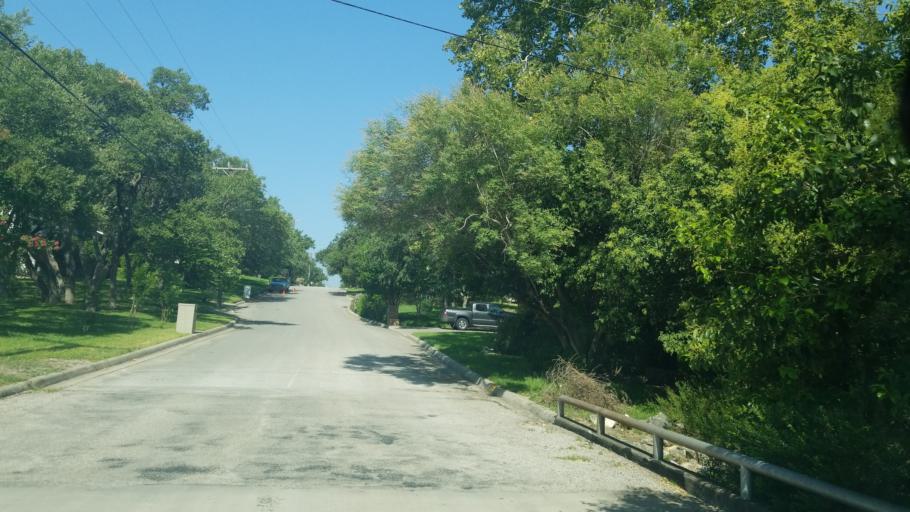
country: US
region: Texas
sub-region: Bexar County
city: Hollywood Park
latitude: 29.6049
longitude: -98.4823
